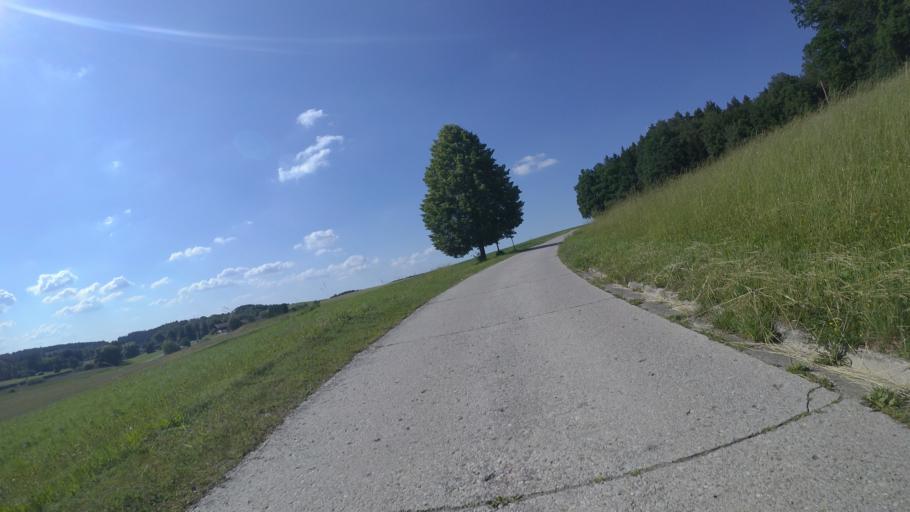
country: DE
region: Bavaria
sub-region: Upper Bavaria
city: Seeon-Seebruck
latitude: 47.9647
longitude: 12.4993
